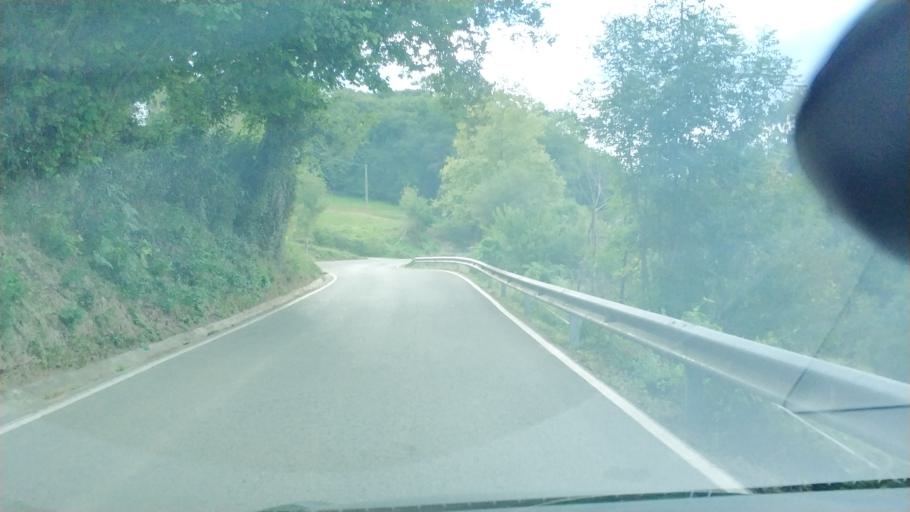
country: ES
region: Cantabria
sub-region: Provincia de Cantabria
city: Santa Maria de Cayon
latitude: 43.2877
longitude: -3.8193
